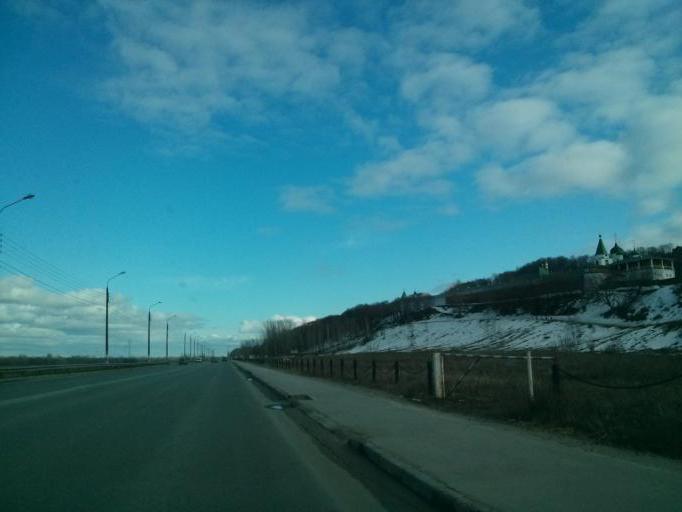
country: RU
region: Nizjnij Novgorod
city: Bor
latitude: 56.3260
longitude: 44.0465
